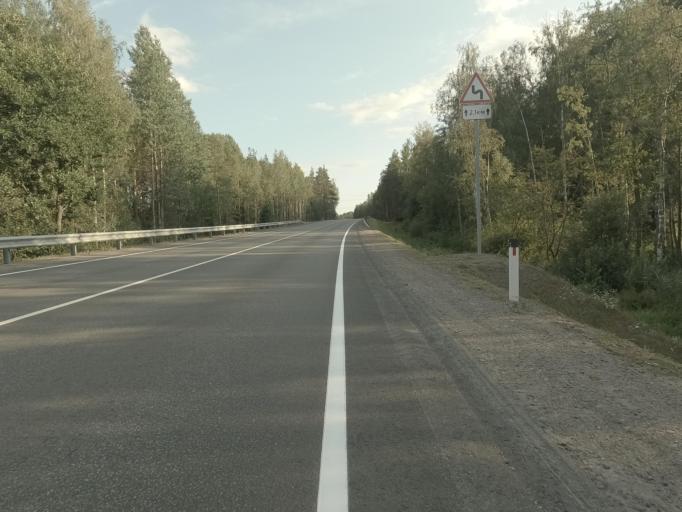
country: RU
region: Leningrad
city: Vyborg
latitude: 60.7827
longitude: 28.8139
